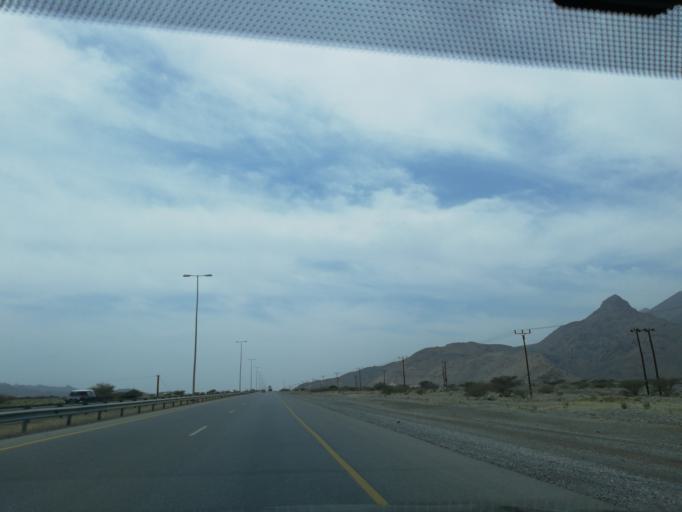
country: OM
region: Muhafazat ad Dakhiliyah
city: Izki
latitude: 23.0807
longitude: 57.8197
